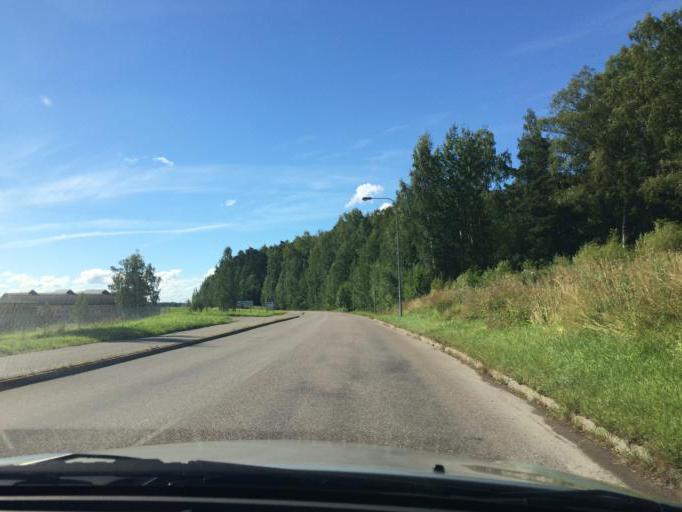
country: SE
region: Vaestmanland
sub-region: Vasteras
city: Vasteras
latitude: 59.5969
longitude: 16.6241
